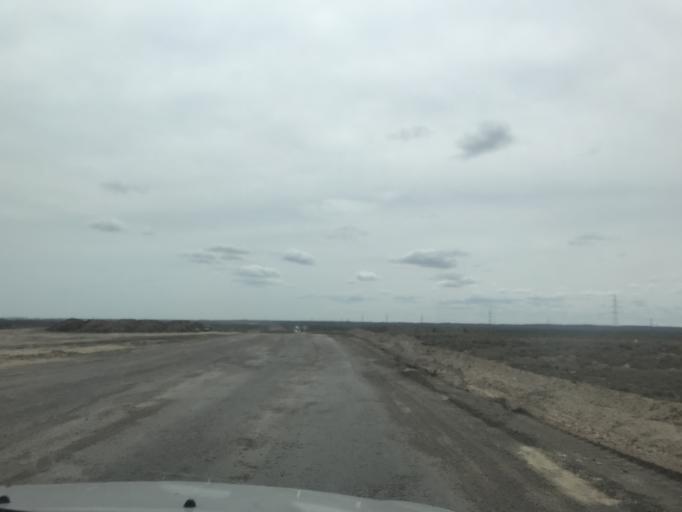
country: KZ
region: Almaty Oblysy
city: Ulken
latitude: 45.2630
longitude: 73.7972
